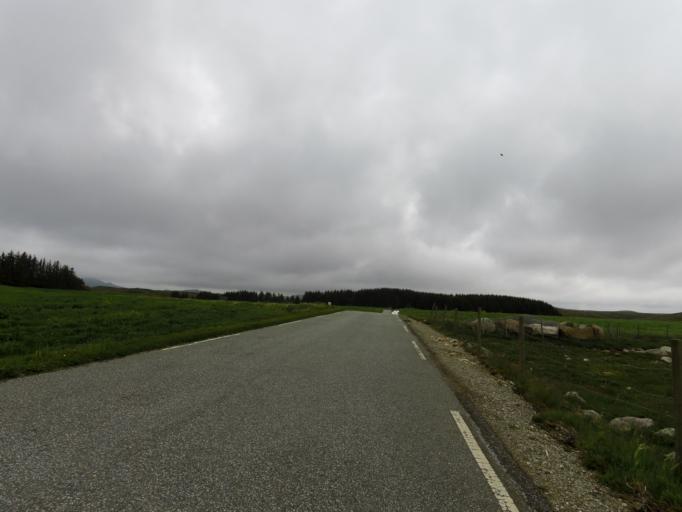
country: NO
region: Rogaland
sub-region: Ha
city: Vigrestad
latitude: 58.6233
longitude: 5.7709
